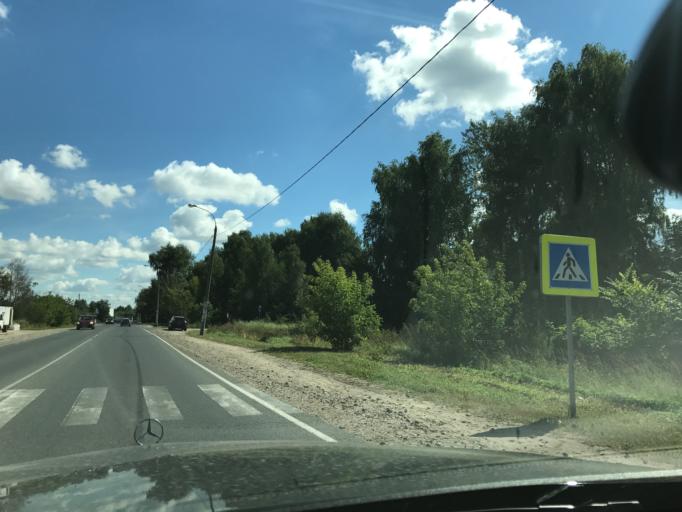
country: RU
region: Nizjnij Novgorod
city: Gorbatovka
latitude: 56.2112
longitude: 43.7650
